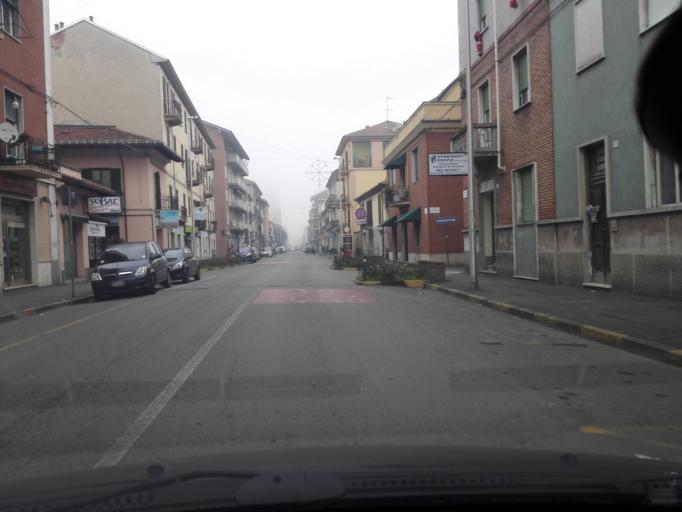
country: IT
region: Piedmont
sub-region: Provincia di Alessandria
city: Alessandria
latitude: 44.8991
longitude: 8.5988
